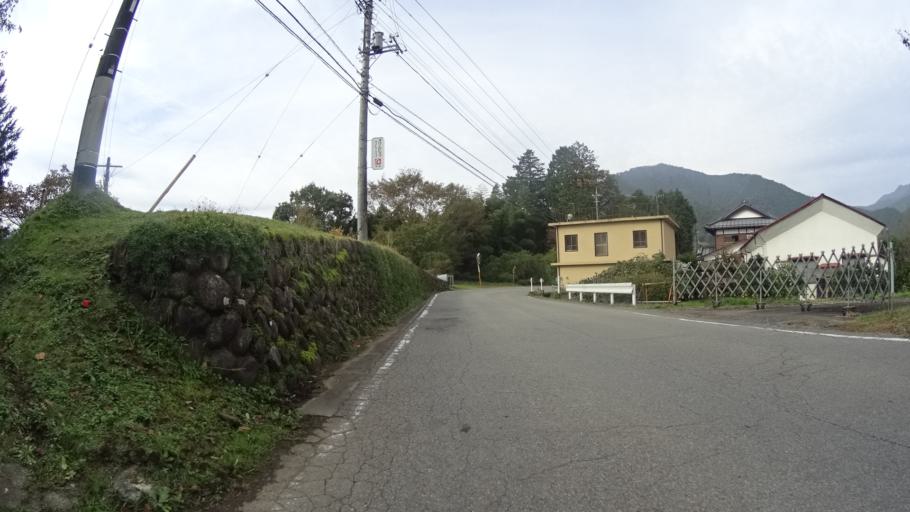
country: JP
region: Yamanashi
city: Uenohara
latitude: 35.6324
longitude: 139.0555
